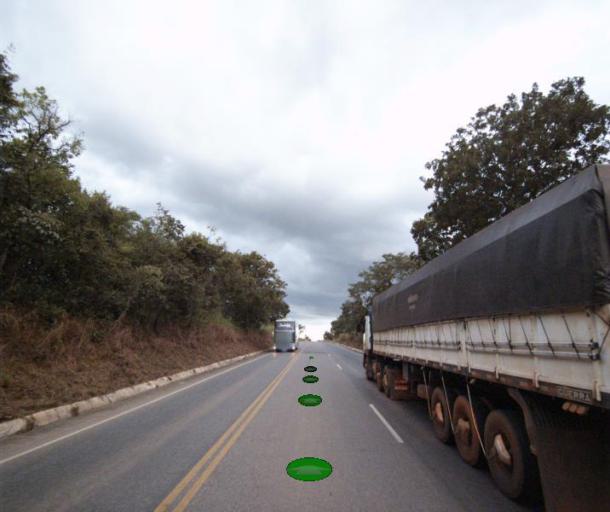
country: BR
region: Goias
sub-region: Uruacu
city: Uruacu
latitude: -14.7151
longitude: -49.2281
